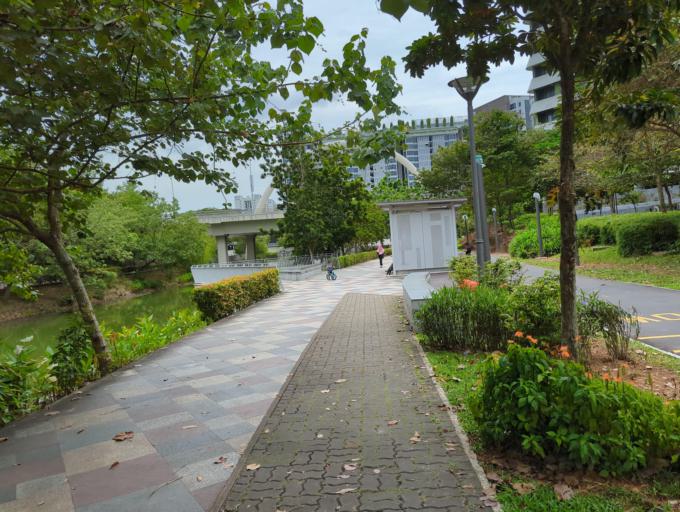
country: MY
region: Johor
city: Kampung Pasir Gudang Baru
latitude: 1.4084
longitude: 103.9007
